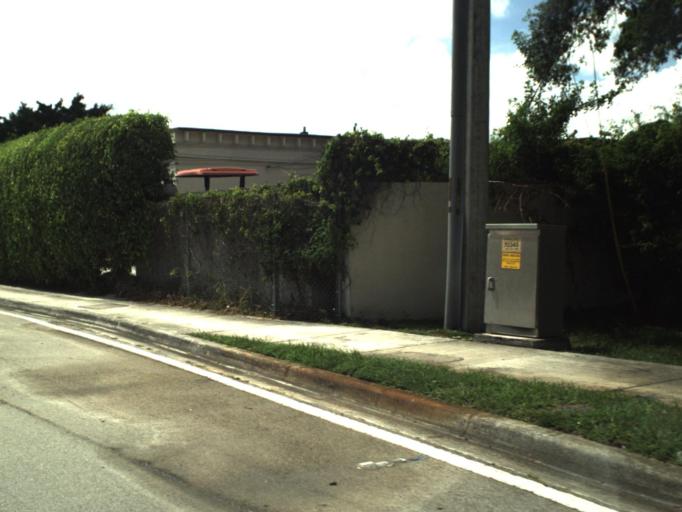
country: US
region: Florida
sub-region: Broward County
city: Miramar
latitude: 25.9942
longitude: -80.2654
